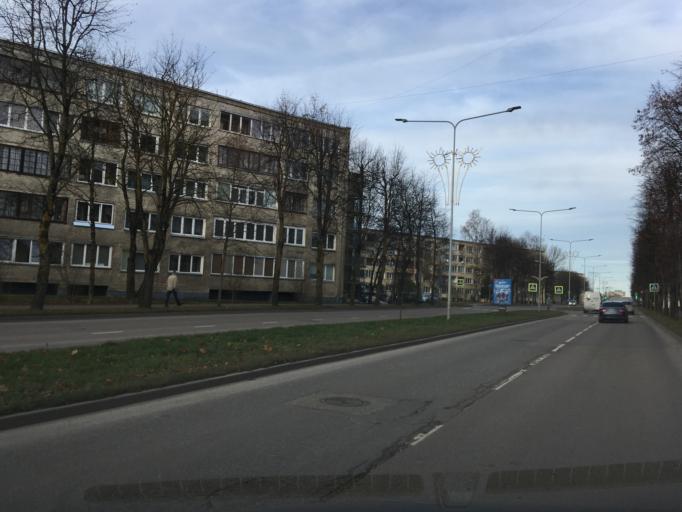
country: EE
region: Ida-Virumaa
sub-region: Narva linn
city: Narva
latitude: 59.3669
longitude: 28.1870
